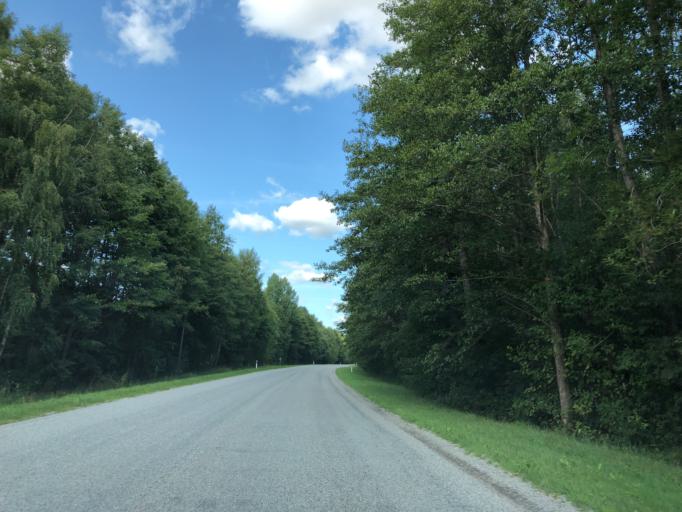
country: EE
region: Hiiumaa
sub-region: Kaerdla linn
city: Kardla
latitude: 58.8196
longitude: 22.7404
